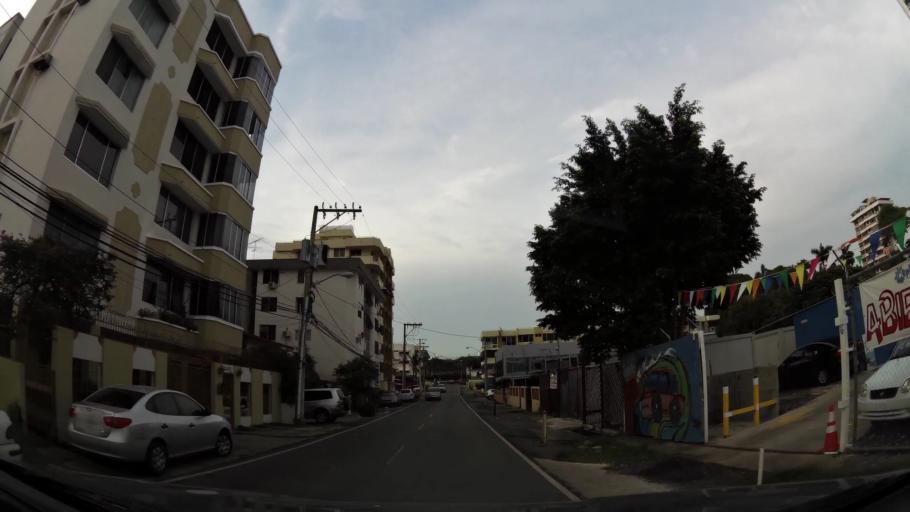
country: PA
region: Panama
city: Panama
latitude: 8.9952
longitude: -79.5086
